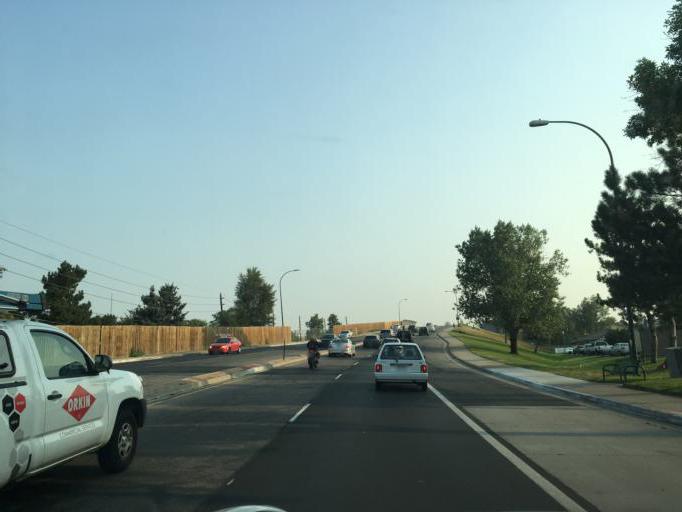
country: US
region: Colorado
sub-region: Adams County
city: Westminster
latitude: 39.8497
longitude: -105.0532
